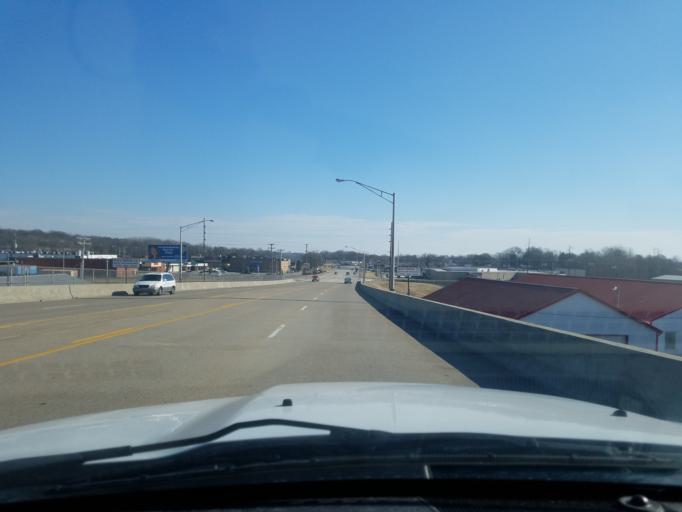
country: US
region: Kentucky
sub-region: Henderson County
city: Henderson
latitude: 37.8341
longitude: -87.5752
